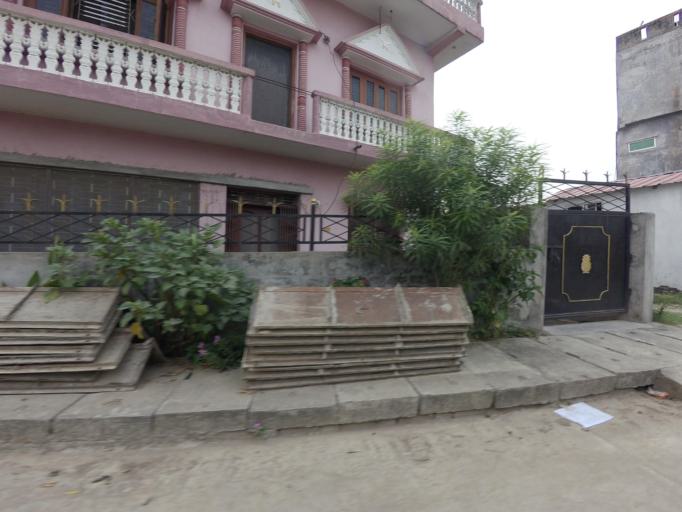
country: NP
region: Western Region
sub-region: Lumbini Zone
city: Bhairahawa
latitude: 27.5207
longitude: 83.4435
